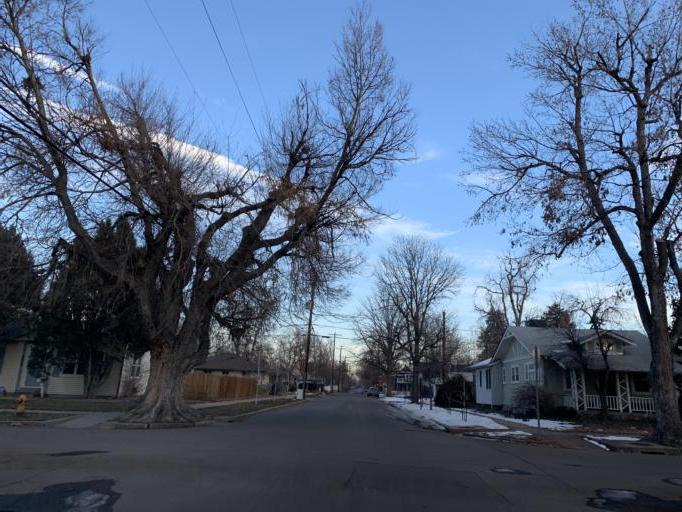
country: US
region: Colorado
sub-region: Jefferson County
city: Edgewater
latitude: 39.7785
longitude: -105.0509
